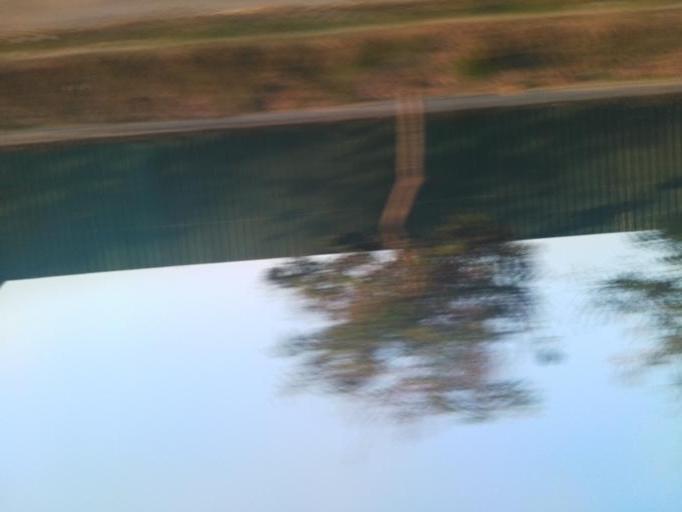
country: TZ
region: Dar es Salaam
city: Dar es Salaam
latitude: -6.8624
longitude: 39.2081
